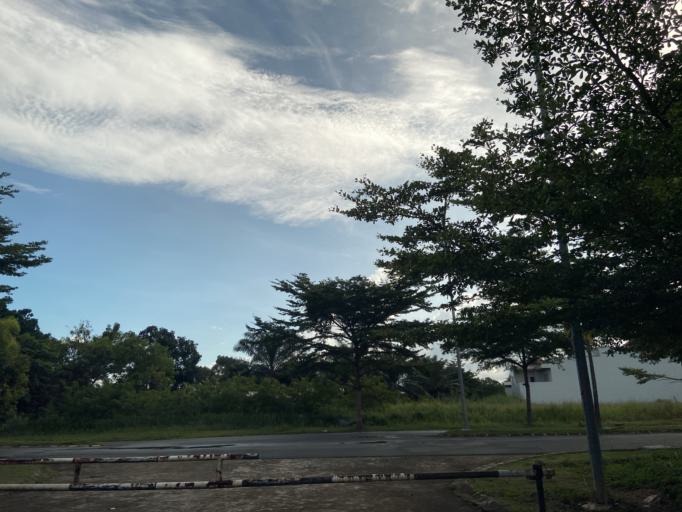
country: SG
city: Singapore
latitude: 1.0907
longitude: 104.0313
